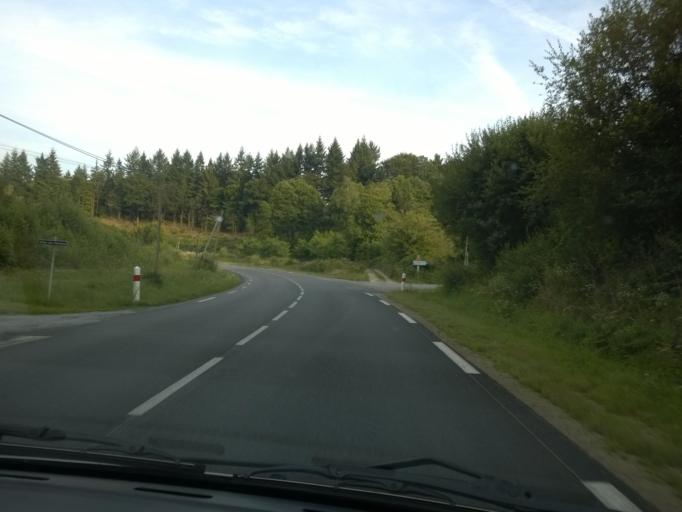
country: FR
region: Limousin
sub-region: Departement de la Haute-Vienne
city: Linards
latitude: 45.7706
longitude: 1.5246
